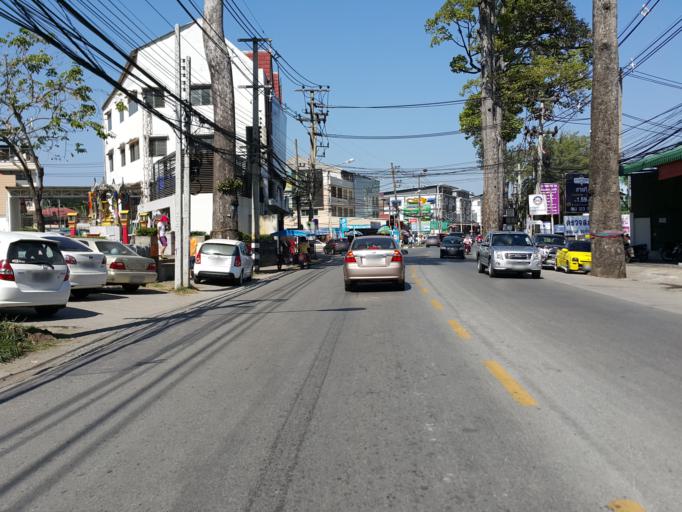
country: TH
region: Chiang Mai
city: Chiang Mai
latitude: 18.7660
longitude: 99.0055
